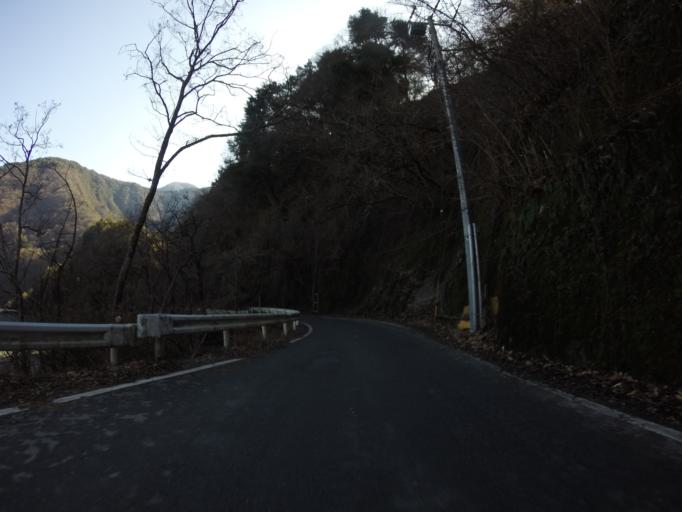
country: JP
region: Yamanashi
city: Ryuo
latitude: 35.4076
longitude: 138.3282
